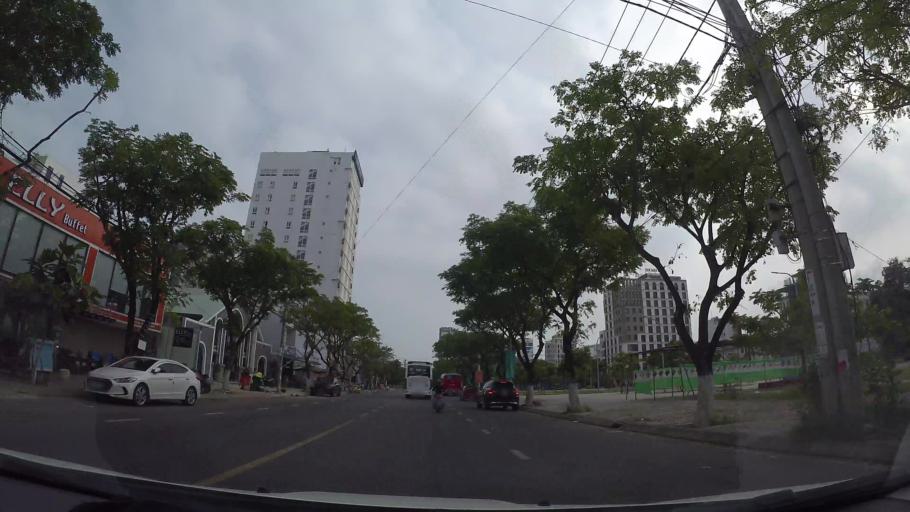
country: VN
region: Da Nang
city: Son Tra
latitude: 16.0766
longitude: 108.2429
